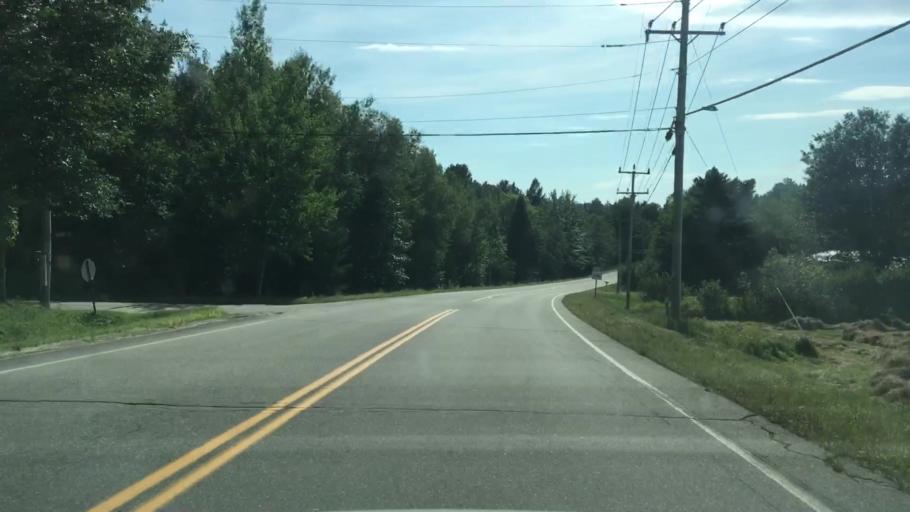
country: US
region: Maine
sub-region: Penobscot County
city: Lincoln
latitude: 45.3964
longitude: -68.5120
